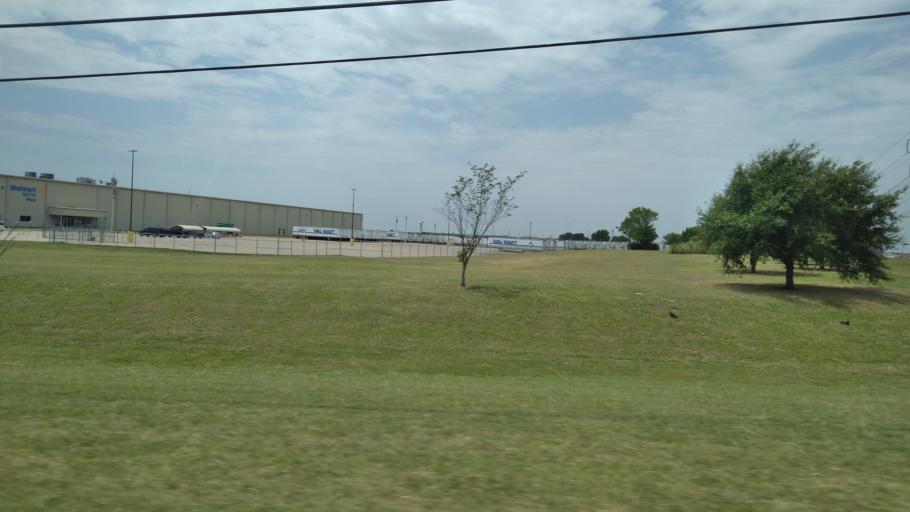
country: US
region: Texas
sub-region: McLennan County
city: Beverly Hills
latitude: 31.4931
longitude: -97.1656
